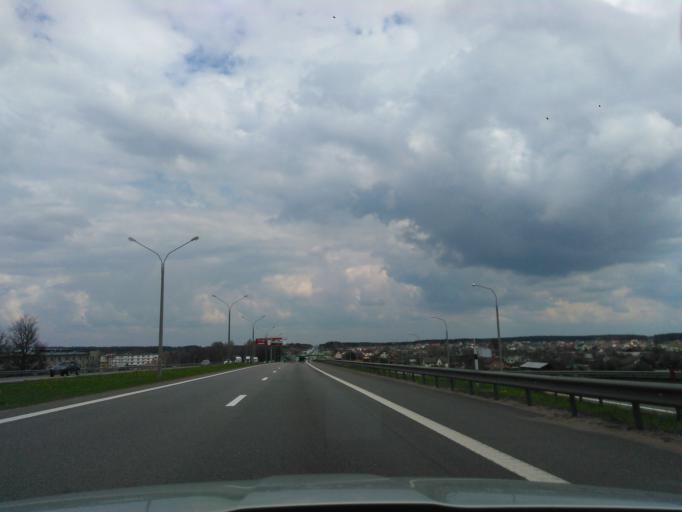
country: BY
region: Minsk
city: Korolev Stan
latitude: 53.9840
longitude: 27.7862
